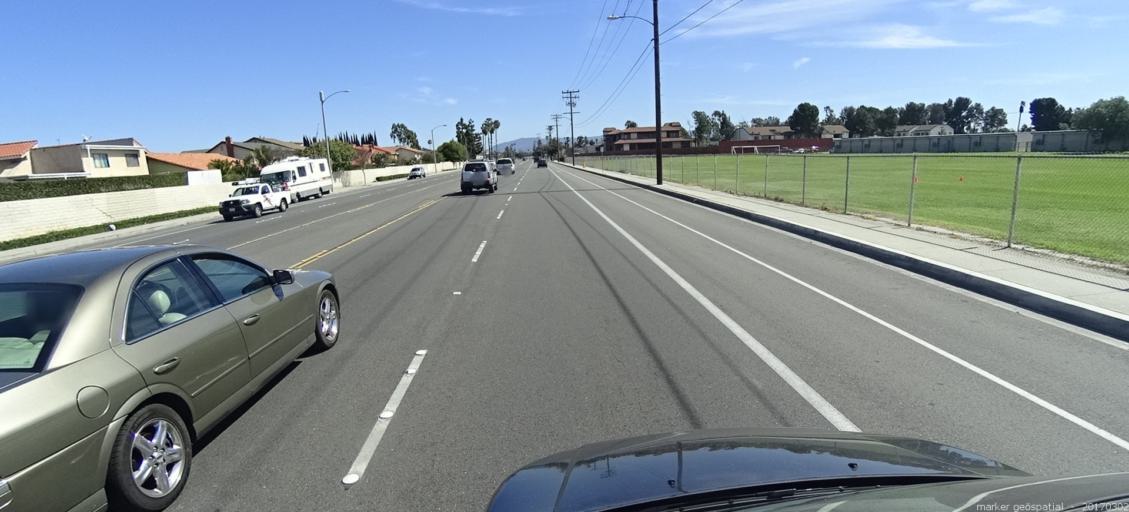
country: US
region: California
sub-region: Orange County
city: Anaheim
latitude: 33.8472
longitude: -117.8932
